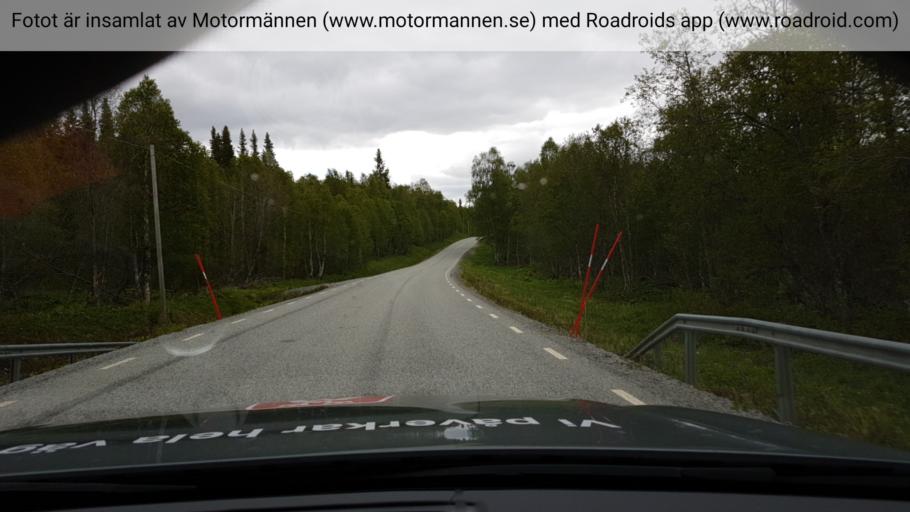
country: NO
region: Nord-Trondelag
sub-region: Royrvik
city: Royrvik
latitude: 64.8456
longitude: 14.0676
